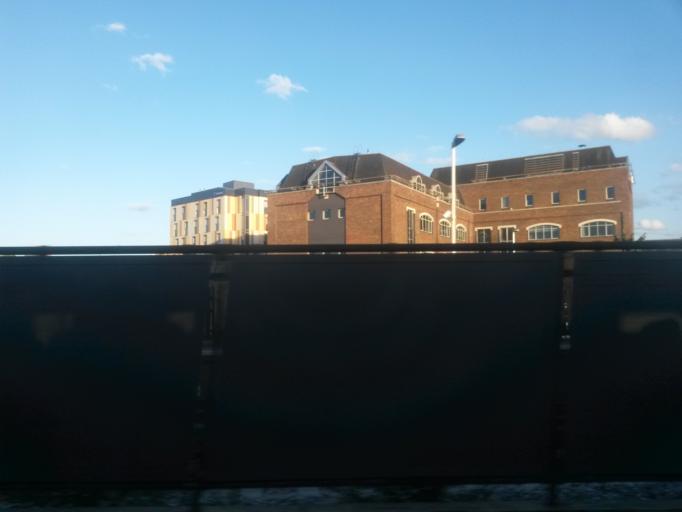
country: GB
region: England
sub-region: Greater London
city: Battersea
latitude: 51.4649
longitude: -0.1689
